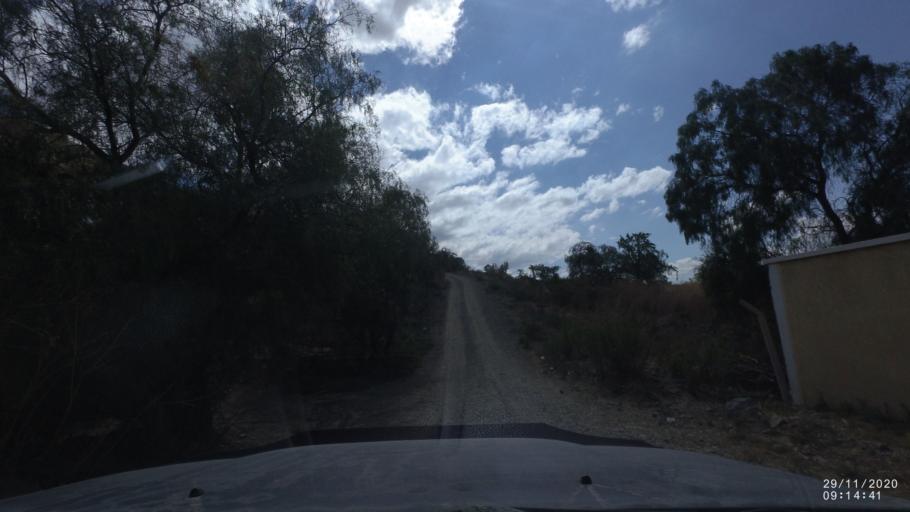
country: BO
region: Cochabamba
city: Cochabamba
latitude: -17.3267
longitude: -66.1918
